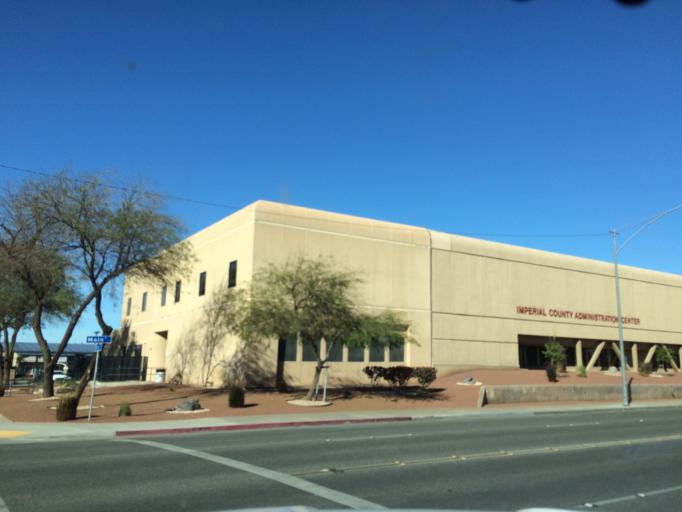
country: US
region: California
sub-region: Imperial County
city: El Centro
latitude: 32.7927
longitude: -115.5644
